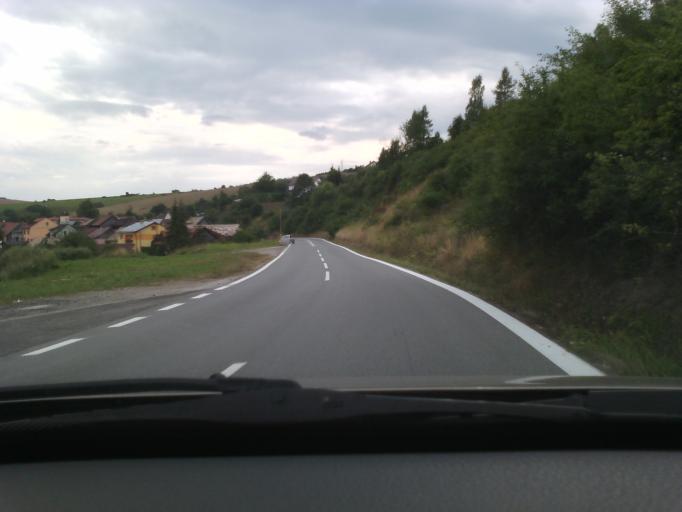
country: SK
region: Presovsky
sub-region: Okres Stara Lubovna
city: Vysne Ruzbachy
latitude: 49.2859
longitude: 20.5795
